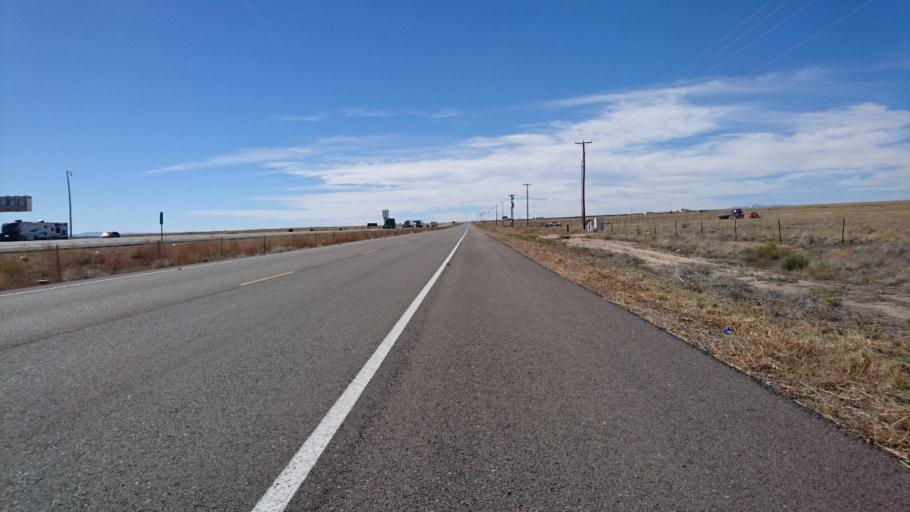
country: US
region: New Mexico
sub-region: Bernalillo County
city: South Valley
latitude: 35.0591
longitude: -106.8133
